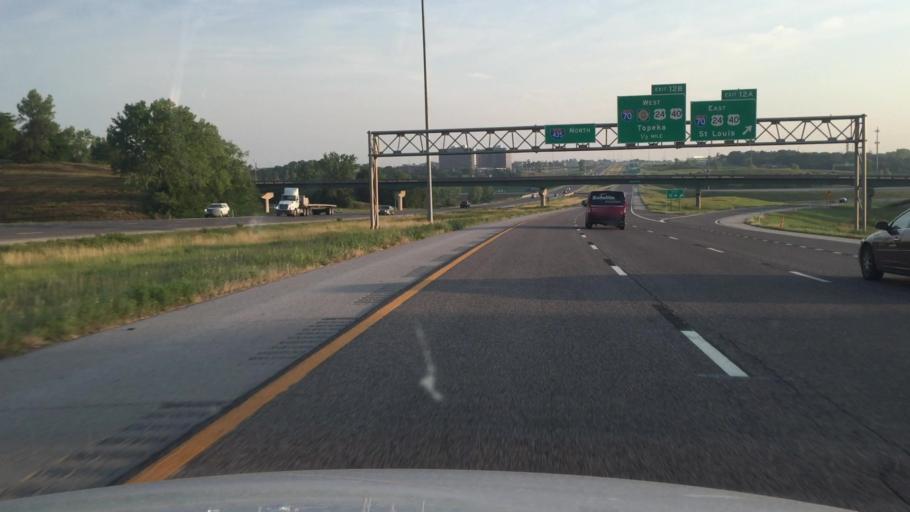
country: US
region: Kansas
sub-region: Wyandotte County
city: Edwardsville
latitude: 39.0996
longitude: -94.8105
